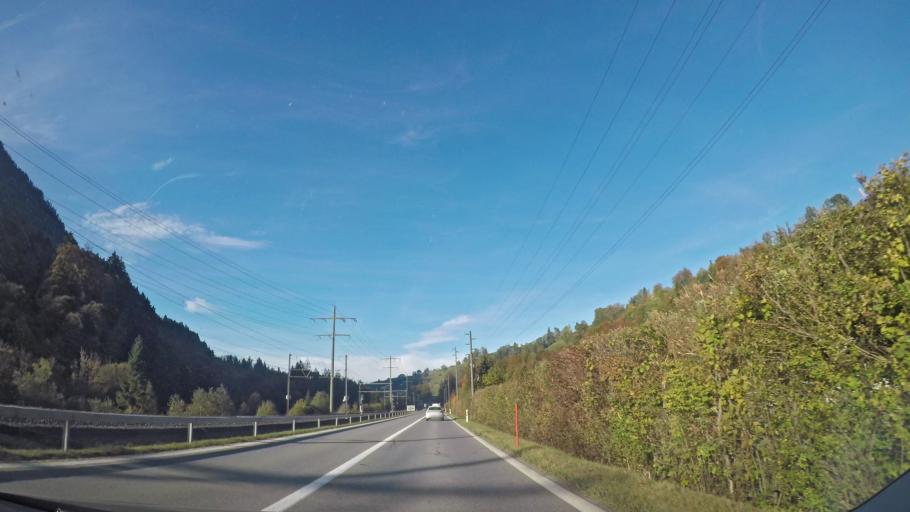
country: CH
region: Bern
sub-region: Frutigen-Niedersimmental District
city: Aeschi
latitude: 46.6416
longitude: 7.6908
